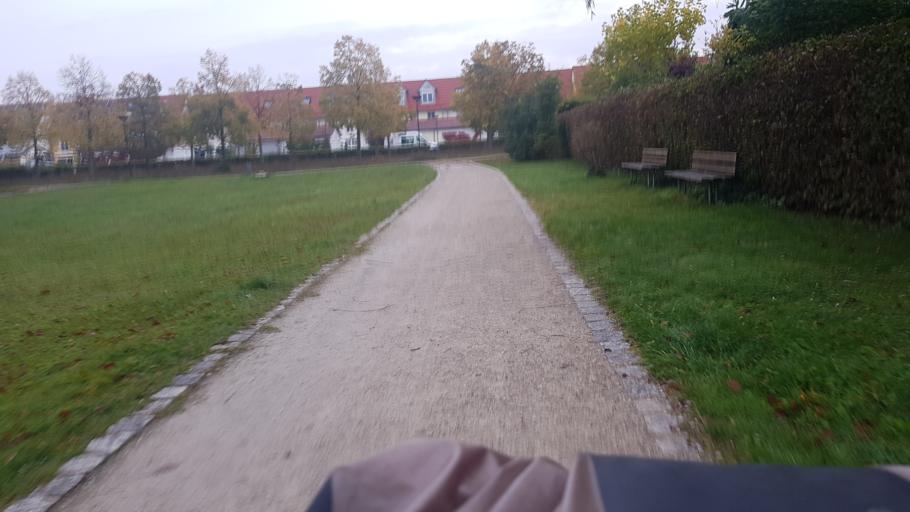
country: DE
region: Bavaria
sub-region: Upper Bavaria
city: Unterhaching
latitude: 48.0851
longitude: 11.6306
